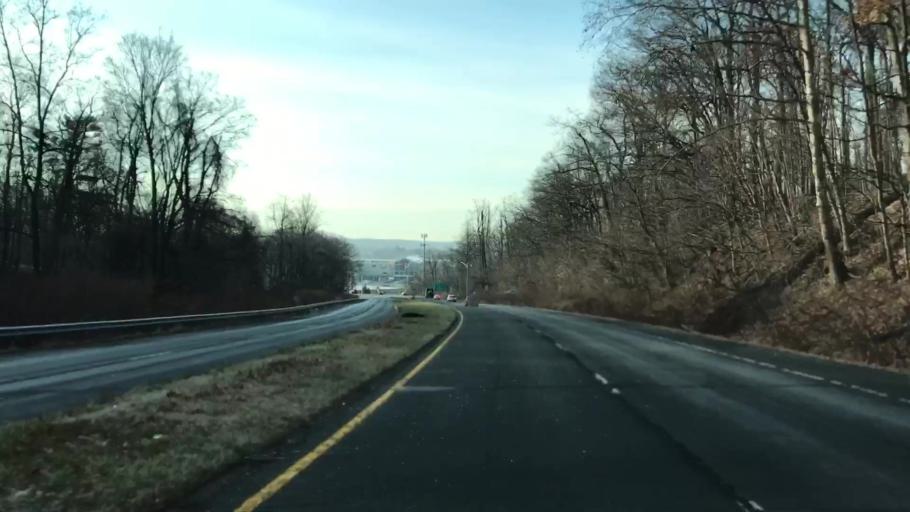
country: US
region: New York
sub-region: Rockland County
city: Valley Cottage
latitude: 41.1065
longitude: -73.9505
